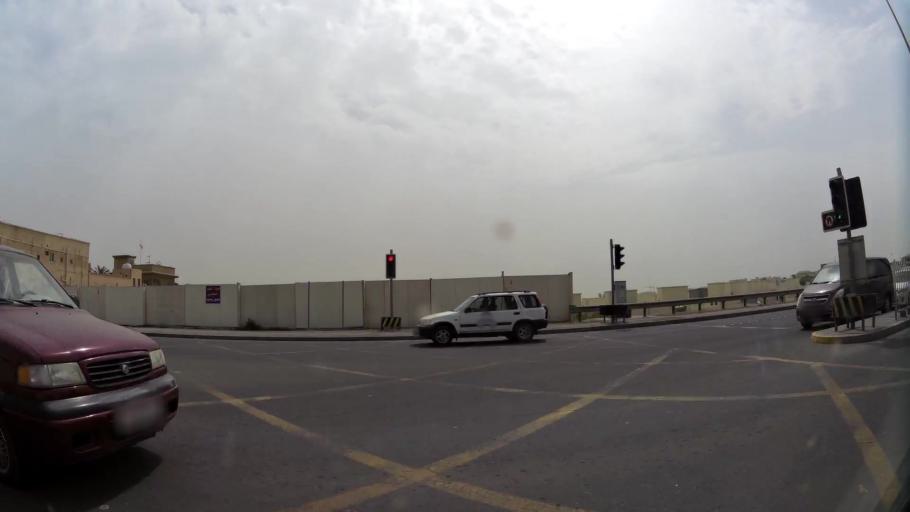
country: BH
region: Northern
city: Ar Rifa'
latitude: 26.1290
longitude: 50.5537
